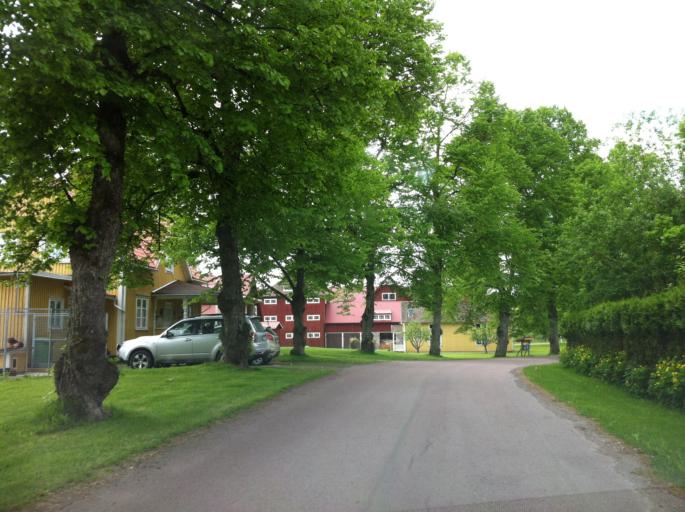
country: SE
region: Vaermland
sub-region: Sunne Kommun
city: Sunne
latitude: 59.9039
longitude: 13.1674
